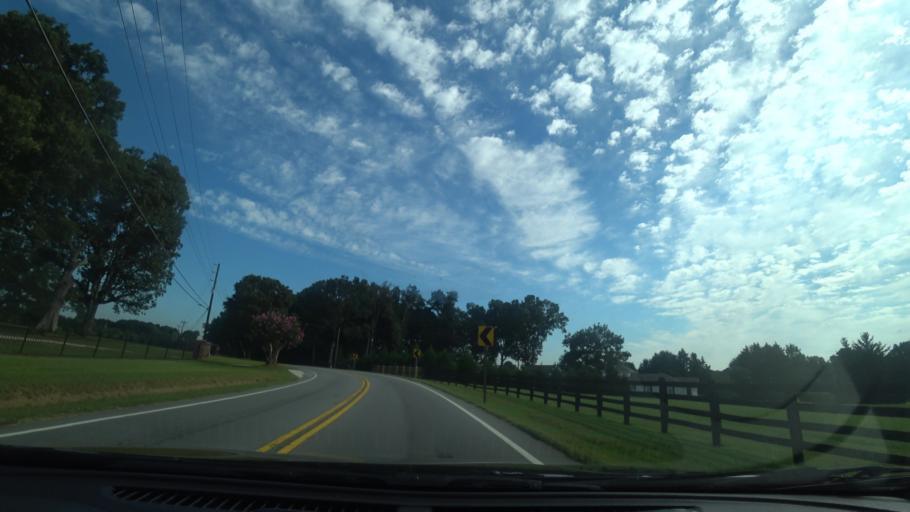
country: US
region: Georgia
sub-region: Walton County
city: Loganville
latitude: 33.8299
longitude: -83.9593
